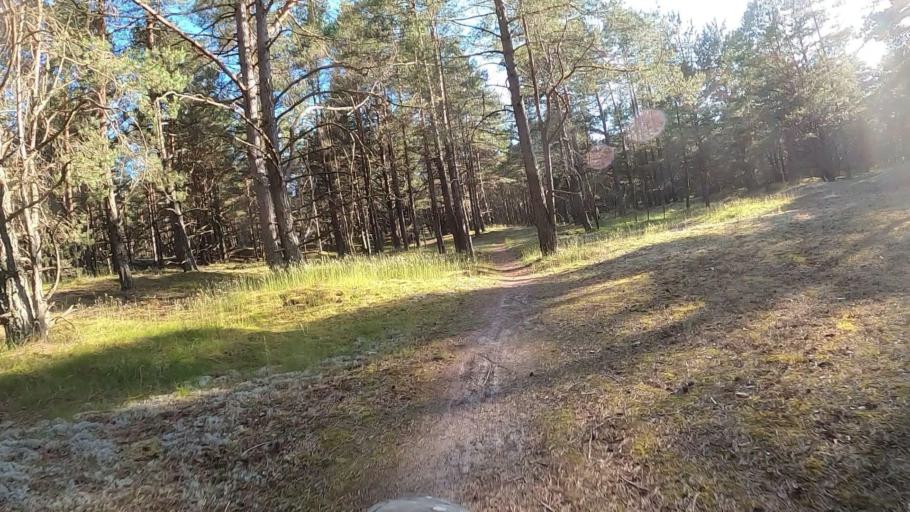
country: LV
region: Carnikava
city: Carnikava
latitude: 57.1323
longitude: 24.2295
